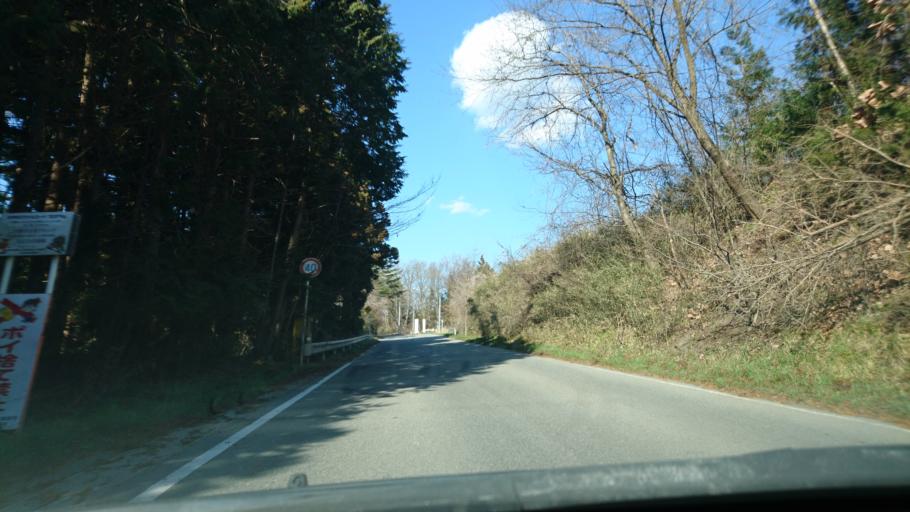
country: JP
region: Iwate
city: Ichinoseki
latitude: 38.7594
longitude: 141.2571
